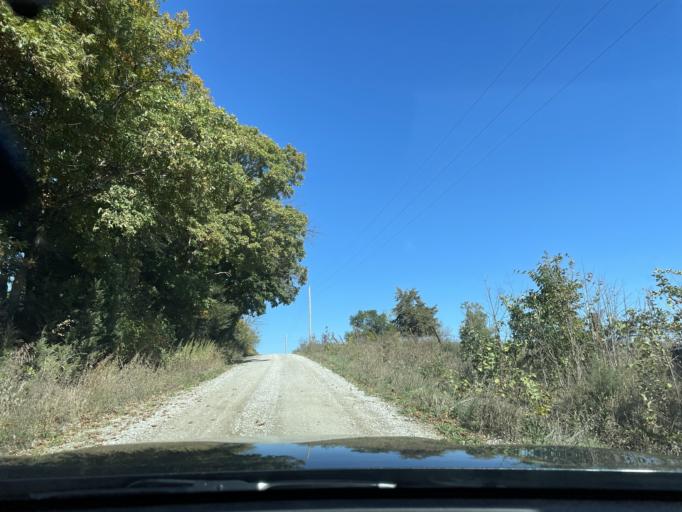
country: US
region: Missouri
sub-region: Andrew County
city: Savannah
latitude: 39.9374
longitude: -94.8803
